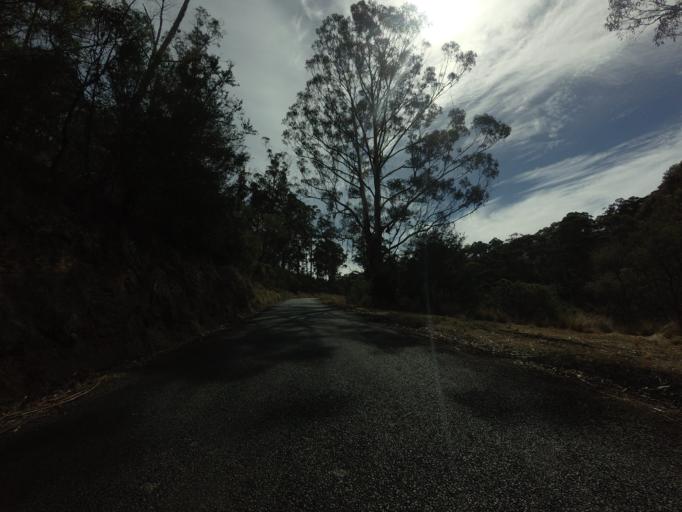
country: AU
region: Tasmania
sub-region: Sorell
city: Sorell
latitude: -42.5640
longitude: 147.6815
